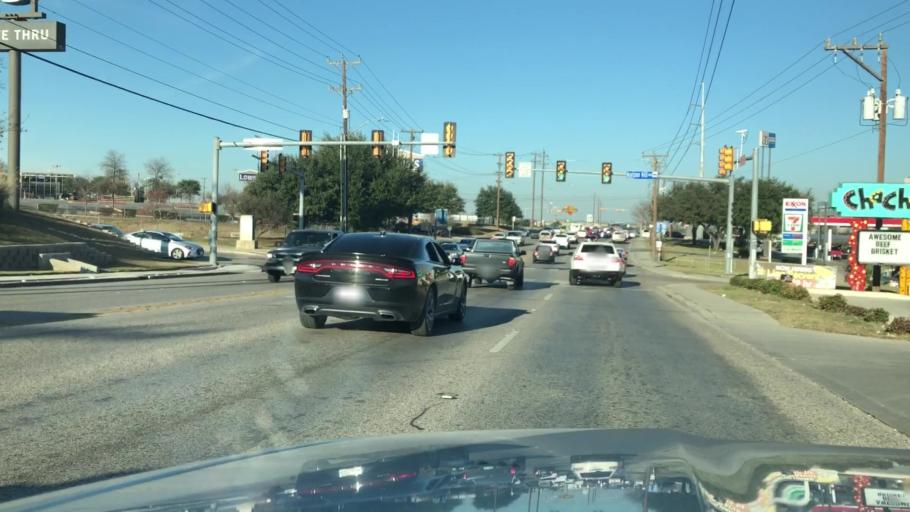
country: US
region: Texas
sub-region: Bexar County
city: Balcones Heights
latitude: 29.5096
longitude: -98.5539
